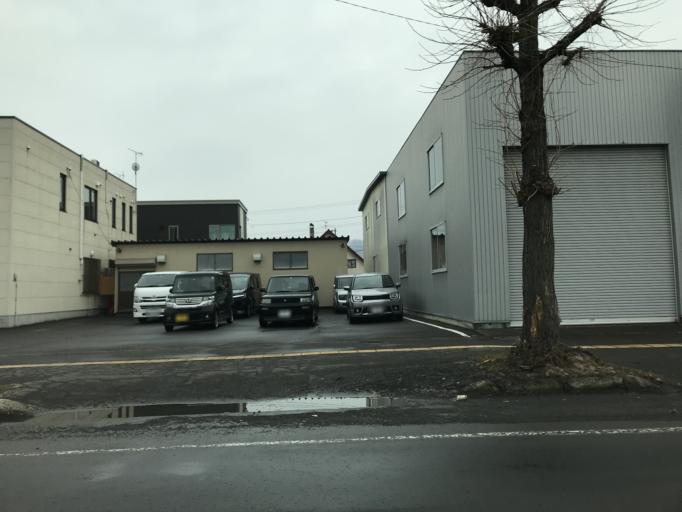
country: JP
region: Hokkaido
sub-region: Asahikawa-shi
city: Asahikawa
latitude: 43.7572
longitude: 142.3366
